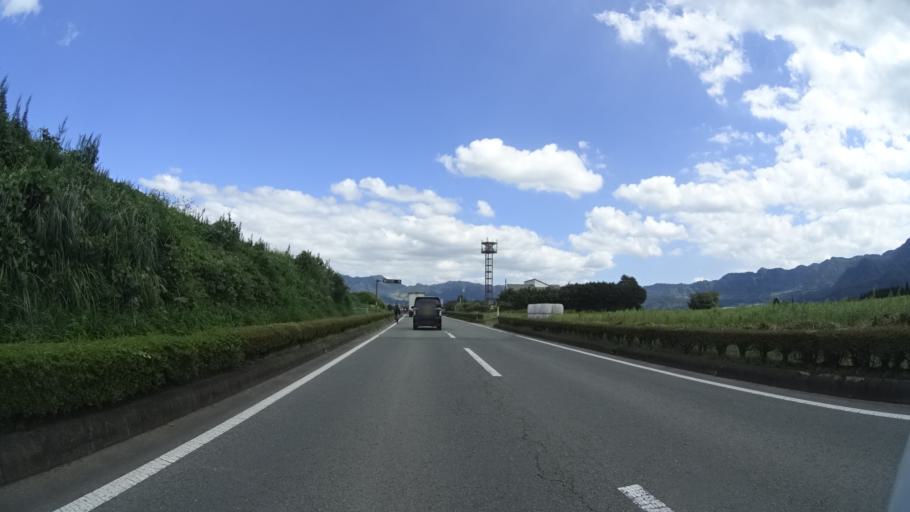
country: JP
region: Kumamoto
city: Aso
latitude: 32.8302
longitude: 131.0878
